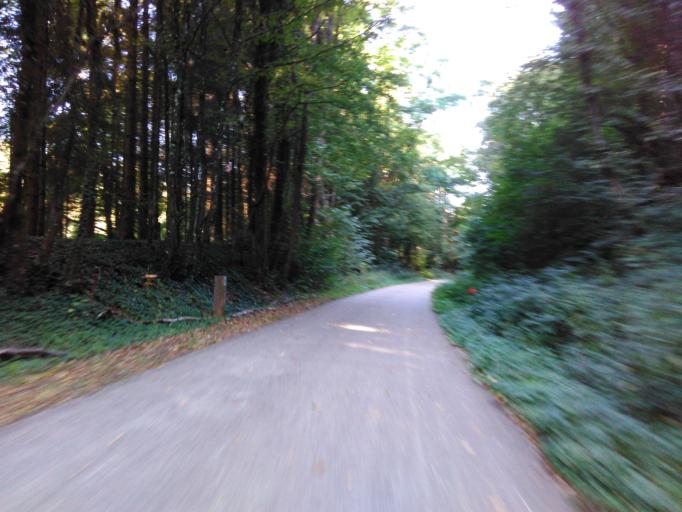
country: LU
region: Diekirch
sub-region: Canton de Redange
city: Beckerich
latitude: 49.7142
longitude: 5.9029
